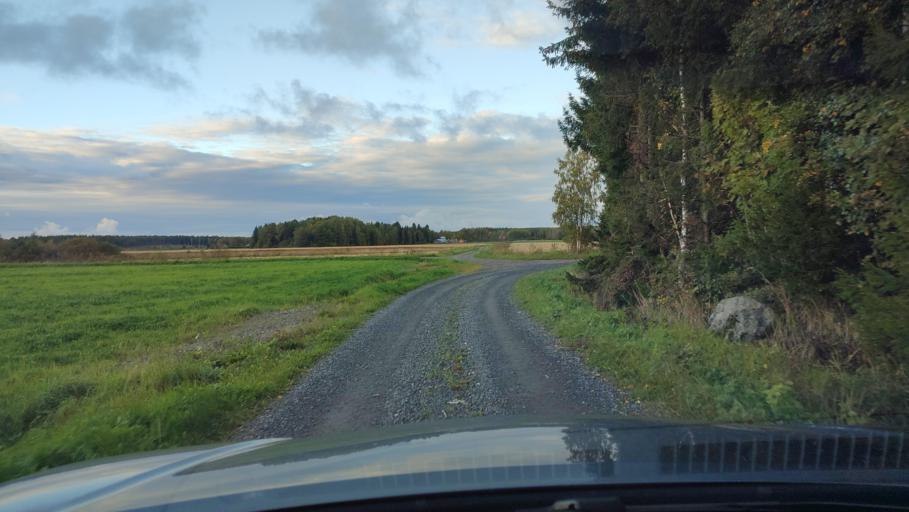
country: FI
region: Ostrobothnia
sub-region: Sydosterbotten
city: Kristinestad
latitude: 62.2512
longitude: 21.4550
